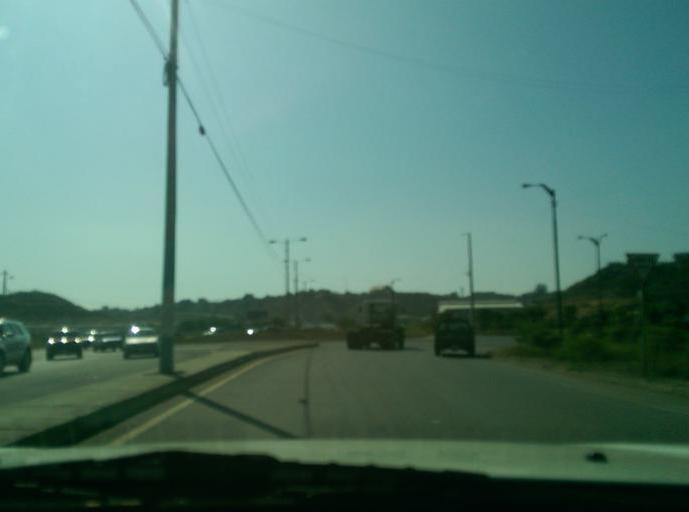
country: EC
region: Manabi
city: Manta
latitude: -0.9645
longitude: -80.7349
